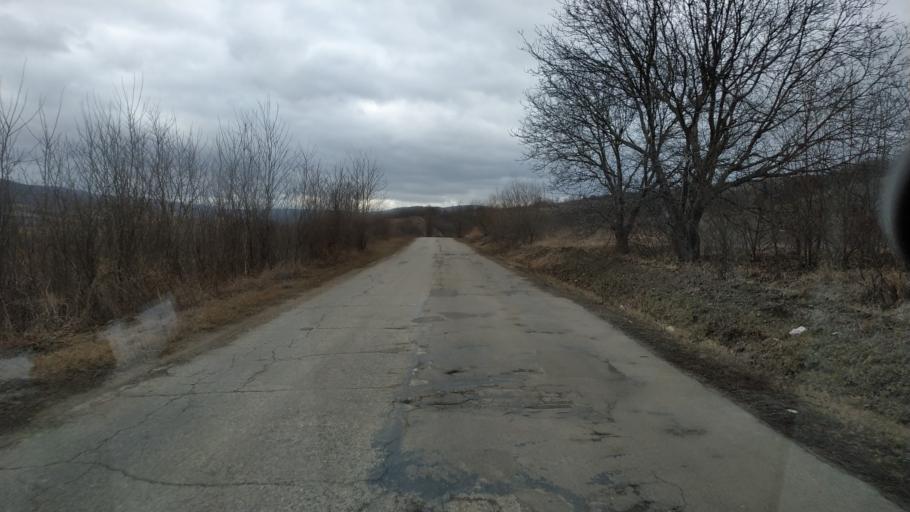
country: MD
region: Calarasi
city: Calarasi
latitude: 47.2386
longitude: 28.1873
